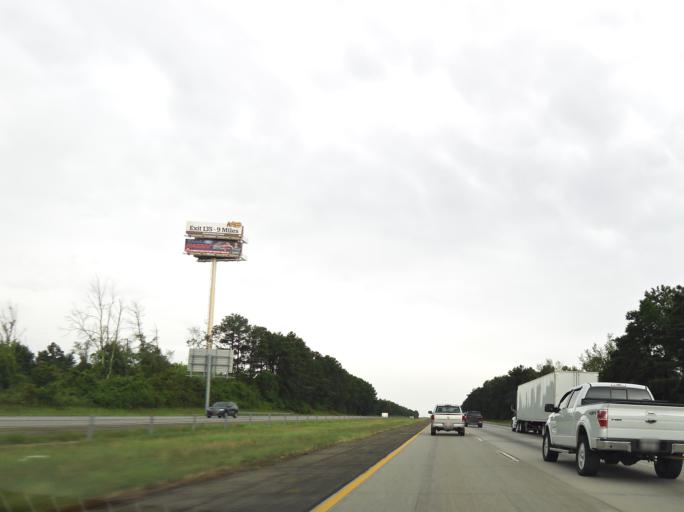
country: US
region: Georgia
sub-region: Houston County
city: Centerville
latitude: 32.5729
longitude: -83.7436
